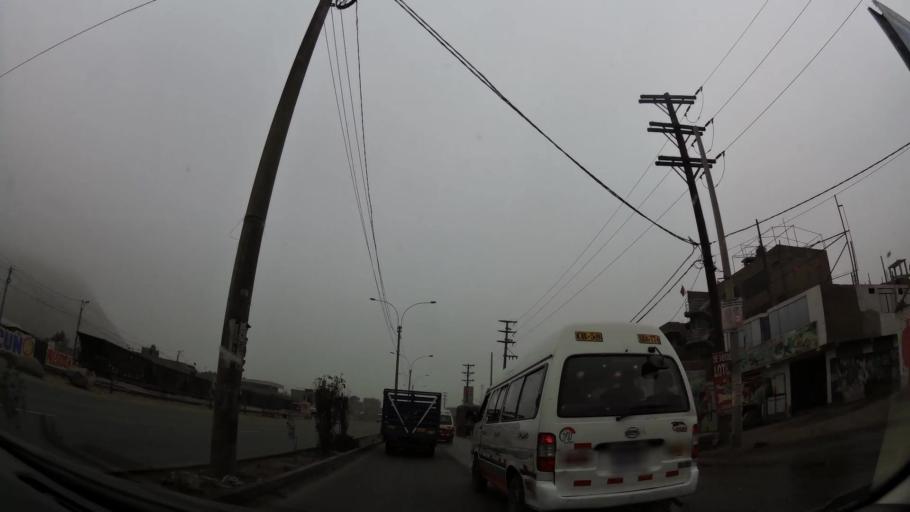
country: PE
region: Lima
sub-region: Lima
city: Santa Maria
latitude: -12.0033
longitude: -76.8427
